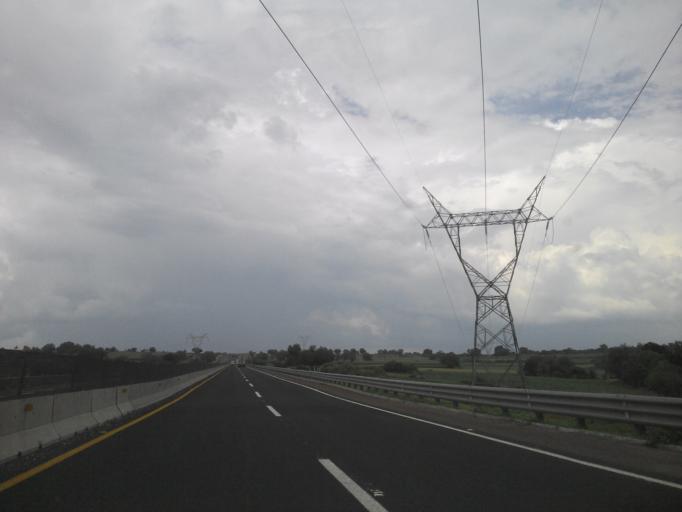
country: MX
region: Hidalgo
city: San Marcos
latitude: 20.0776
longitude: -99.3472
